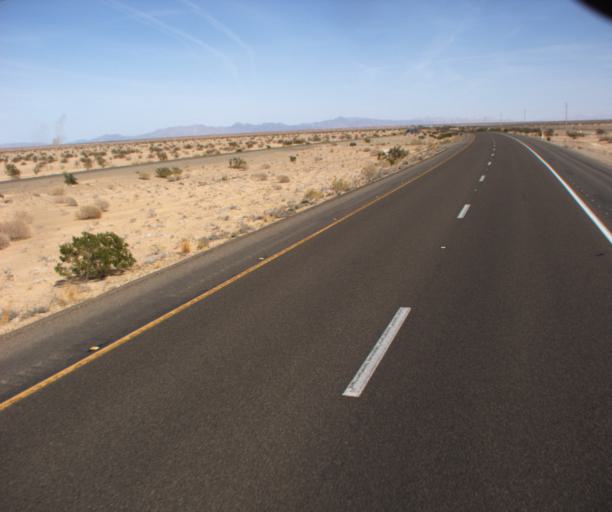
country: US
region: Arizona
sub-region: Yuma County
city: Somerton
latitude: 32.4954
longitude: -114.6422
